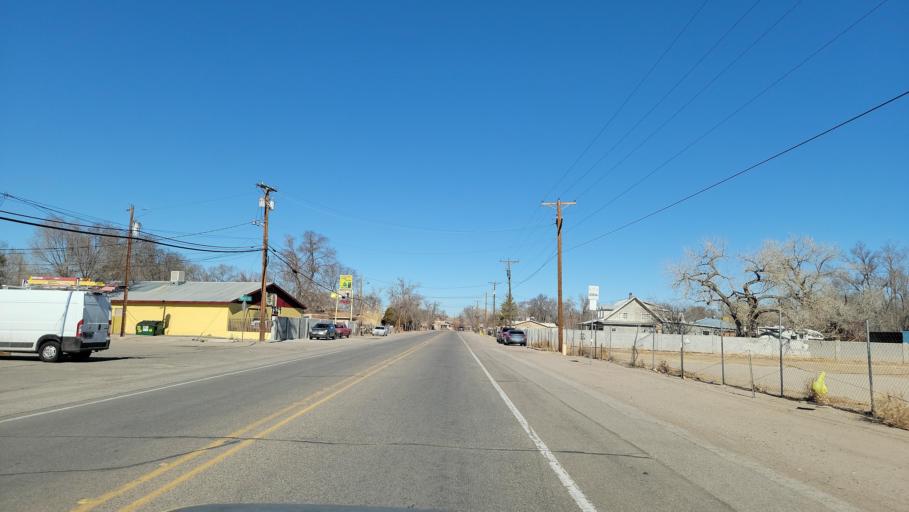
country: US
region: New Mexico
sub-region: Bernalillo County
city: South Valley
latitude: 34.9531
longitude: -106.6949
